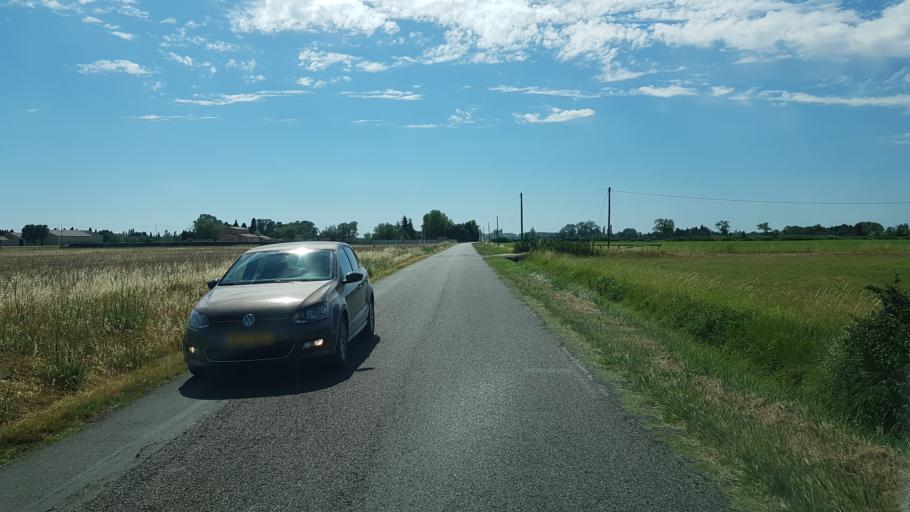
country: FR
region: Provence-Alpes-Cote d'Azur
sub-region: Departement des Bouches-du-Rhone
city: Saint-Martin-de-Crau
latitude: 43.6555
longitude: 4.7705
